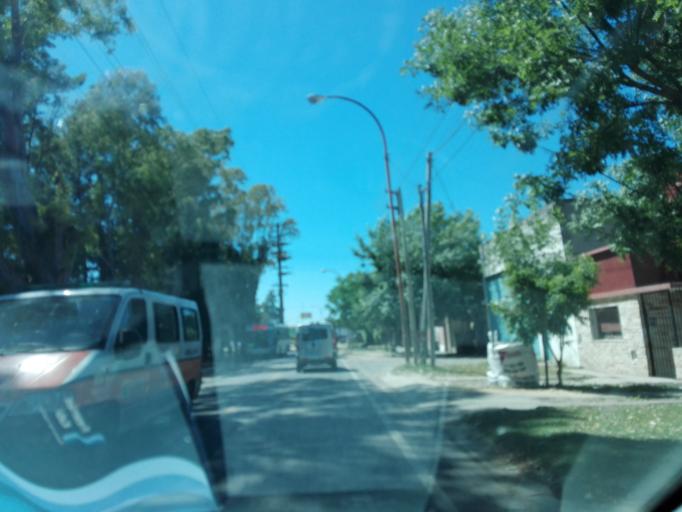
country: AR
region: Buenos Aires
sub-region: Partido de La Plata
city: La Plata
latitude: -34.9002
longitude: -57.9239
